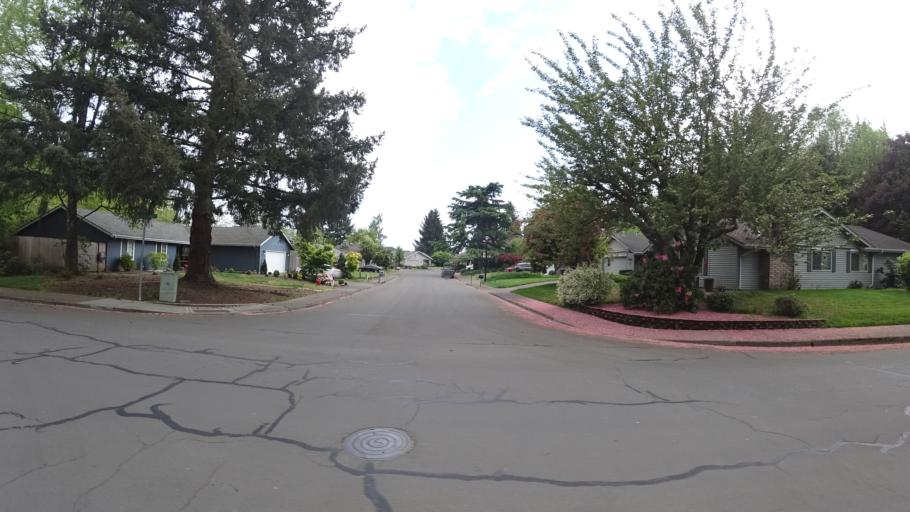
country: US
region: Oregon
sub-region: Washington County
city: Hillsboro
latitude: 45.4937
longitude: -122.9533
